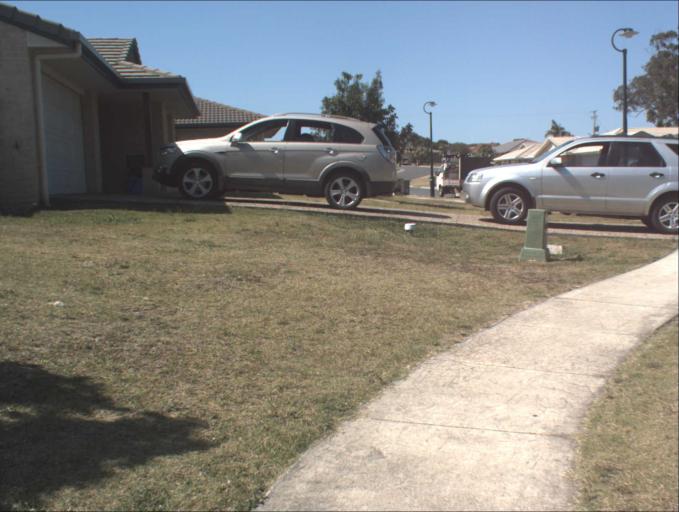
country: AU
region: Queensland
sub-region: Gold Coast
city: Yatala
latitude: -27.6975
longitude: 153.2204
